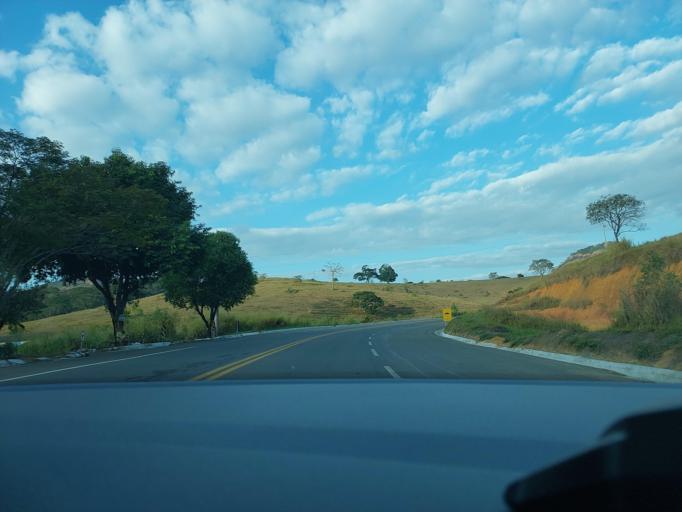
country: BR
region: Minas Gerais
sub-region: Muriae
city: Muriae
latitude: -21.1260
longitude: -42.3296
